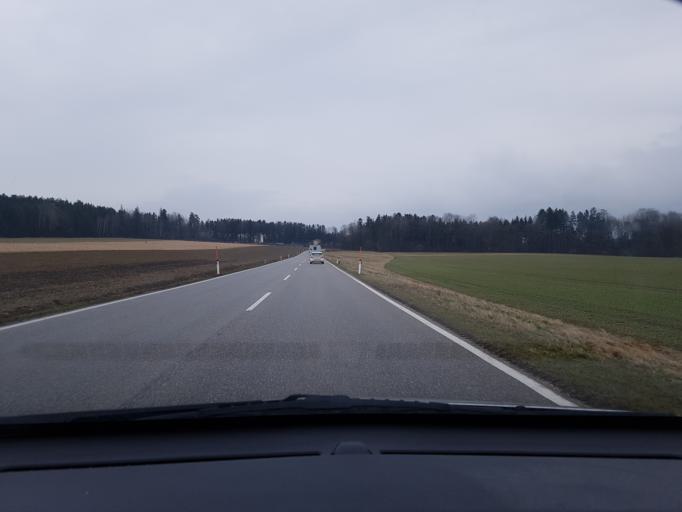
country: AT
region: Upper Austria
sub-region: Steyr Stadt
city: Steyr
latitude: 48.0670
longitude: 14.3858
